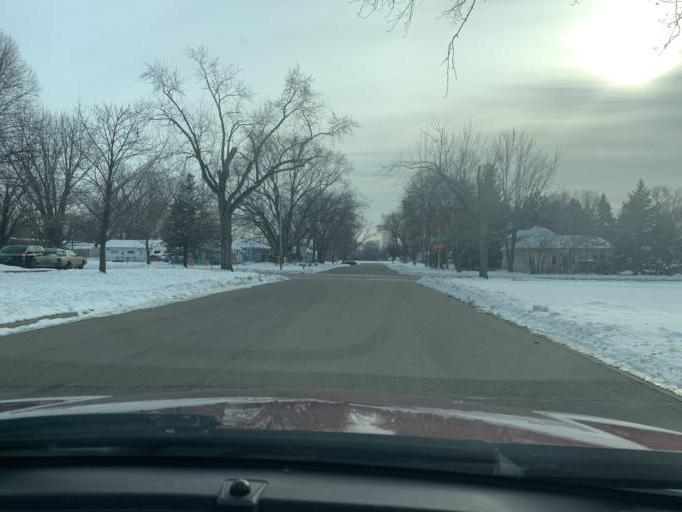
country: US
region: Minnesota
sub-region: Washington County
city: Saint Paul Park
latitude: 44.8371
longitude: -92.9871
